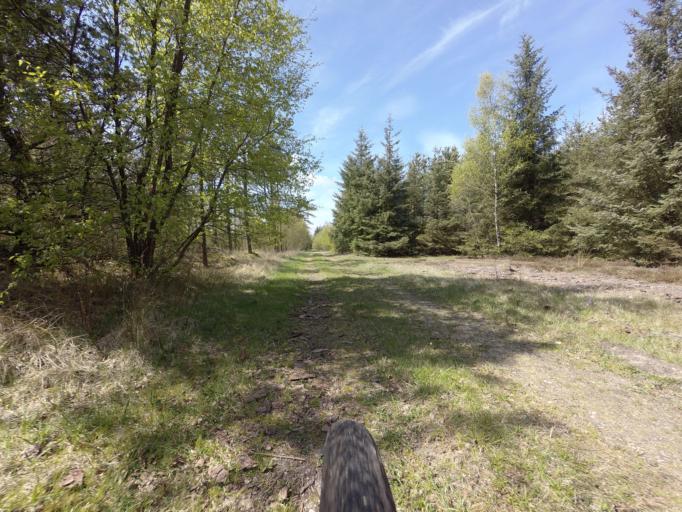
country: DK
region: North Denmark
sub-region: Jammerbugt Kommune
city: Brovst
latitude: 57.1659
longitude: 9.5587
